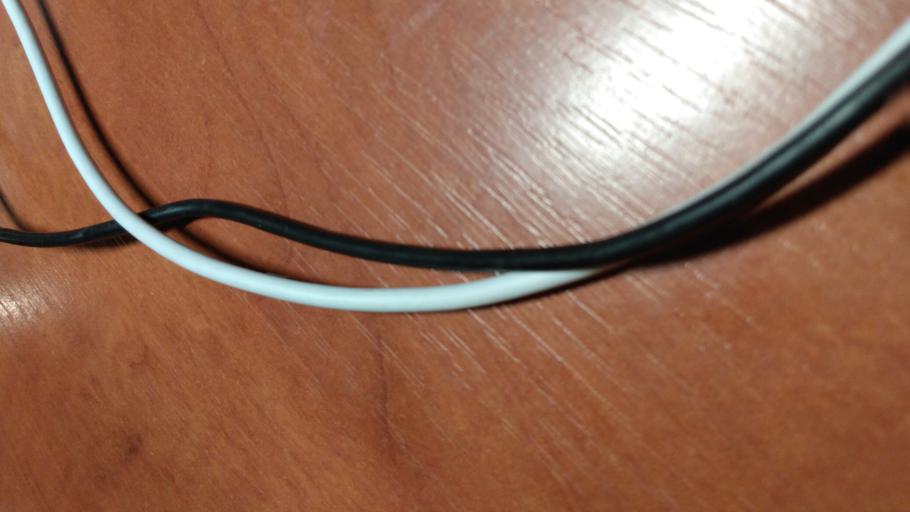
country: RU
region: Republic of Karelia
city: Pudozh
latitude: 61.9947
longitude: 37.6014
